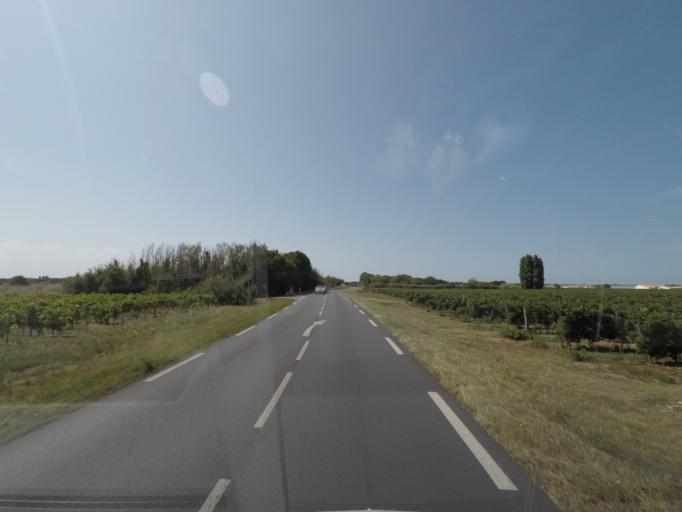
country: FR
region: Poitou-Charentes
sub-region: Departement de la Charente-Maritime
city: Le Bois-Plage-en-Re
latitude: 46.2006
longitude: -1.3966
